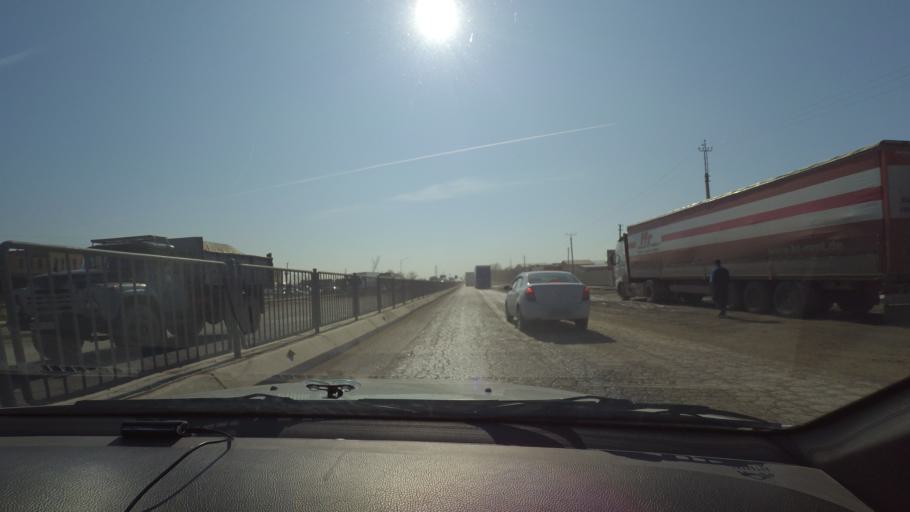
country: UZ
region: Bukhara
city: Bukhara
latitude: 39.8068
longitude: 64.4218
